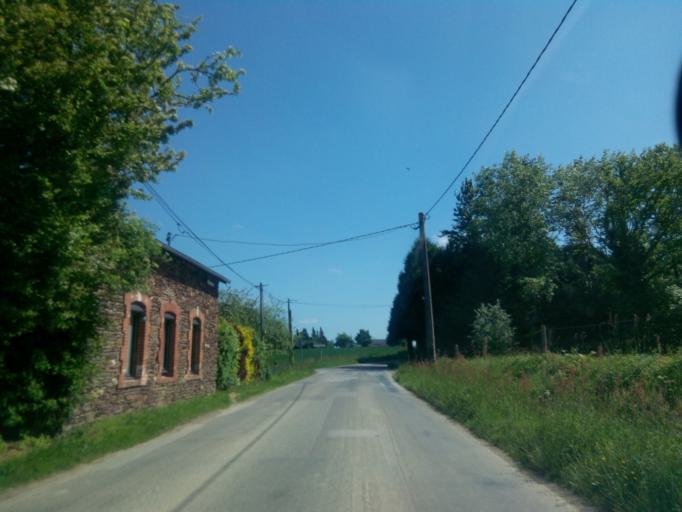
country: FR
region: Brittany
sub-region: Departement d'Ille-et-Vilaine
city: Cesson-Sevigne
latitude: 48.1402
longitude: -1.6030
